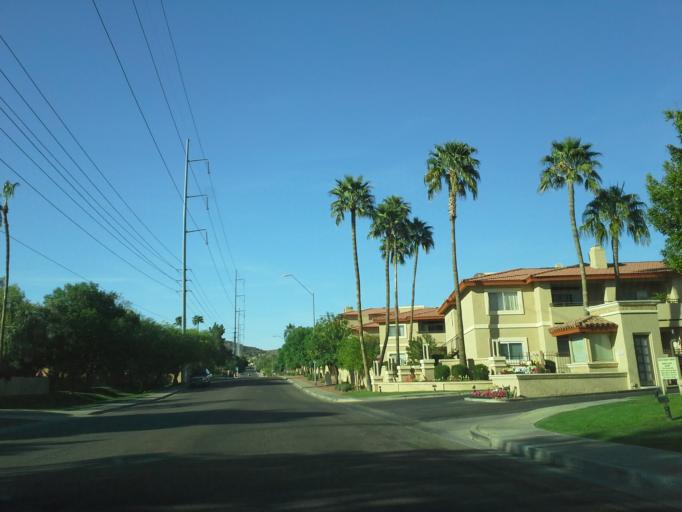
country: US
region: Arizona
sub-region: Maricopa County
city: Paradise Valley
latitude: 33.5804
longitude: -112.0565
